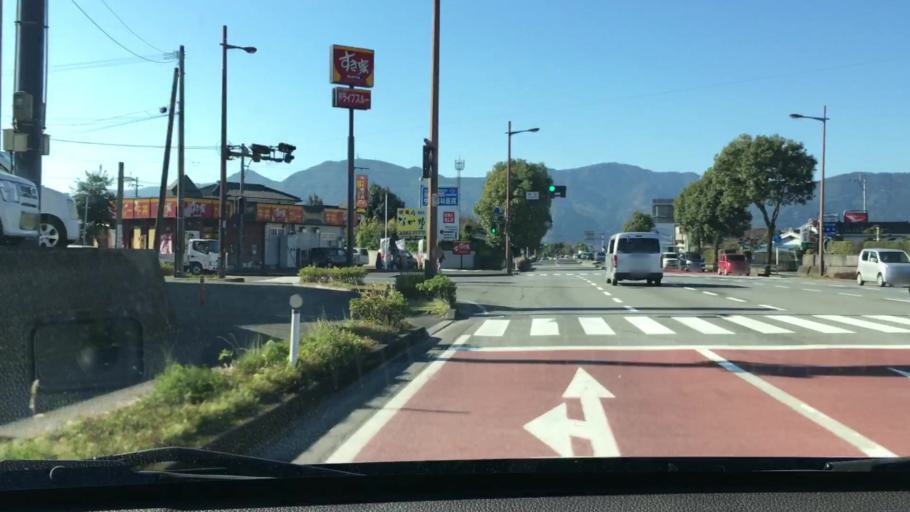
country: JP
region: Kagoshima
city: Kajiki
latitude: 31.7313
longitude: 130.6289
